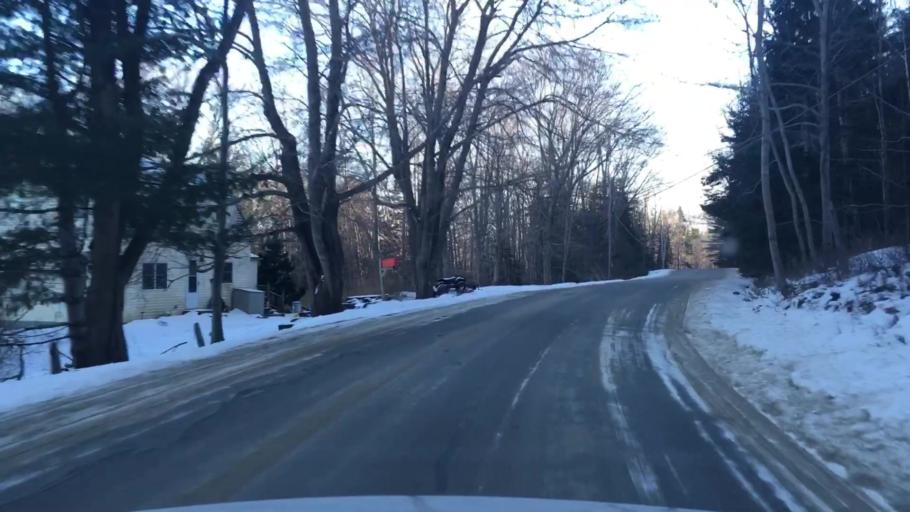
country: US
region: Maine
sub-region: Hancock County
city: Castine
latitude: 44.3475
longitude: -68.7823
